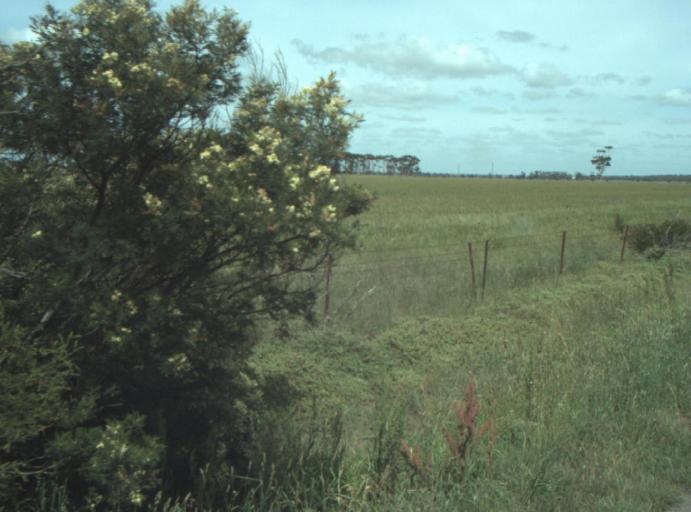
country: AU
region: Victoria
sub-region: Wyndham
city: Little River
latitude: -37.9598
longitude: 144.4876
